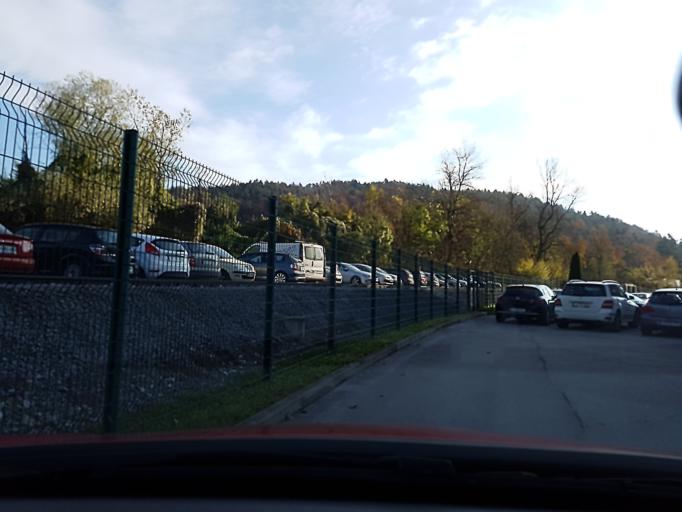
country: SI
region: Trzin
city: Trzin
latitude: 46.0951
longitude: 14.5573
